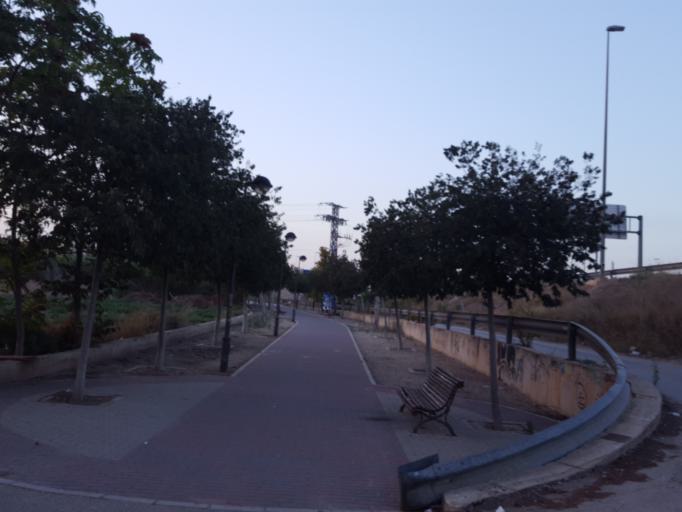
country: ES
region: Murcia
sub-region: Murcia
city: Murcia
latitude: 37.9779
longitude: -1.1370
